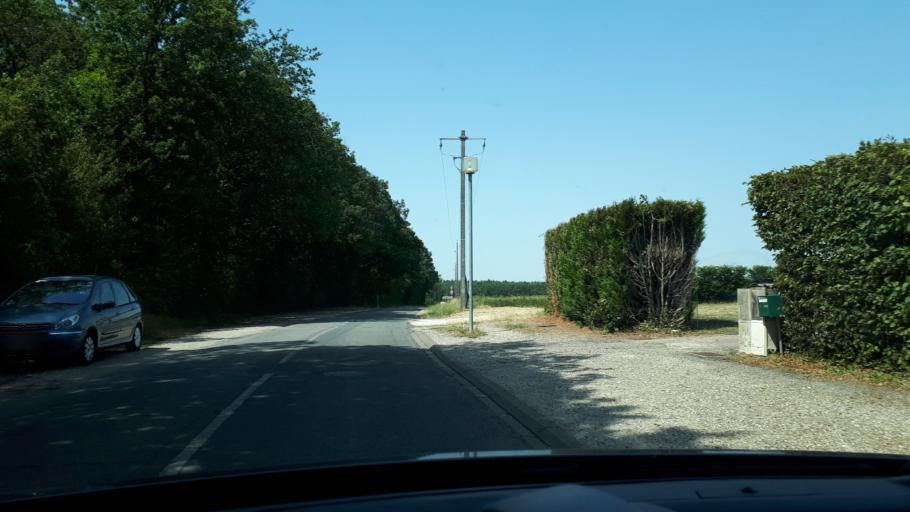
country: FR
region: Centre
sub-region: Departement du Loir-et-Cher
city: Naveil
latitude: 47.8156
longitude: 1.0471
